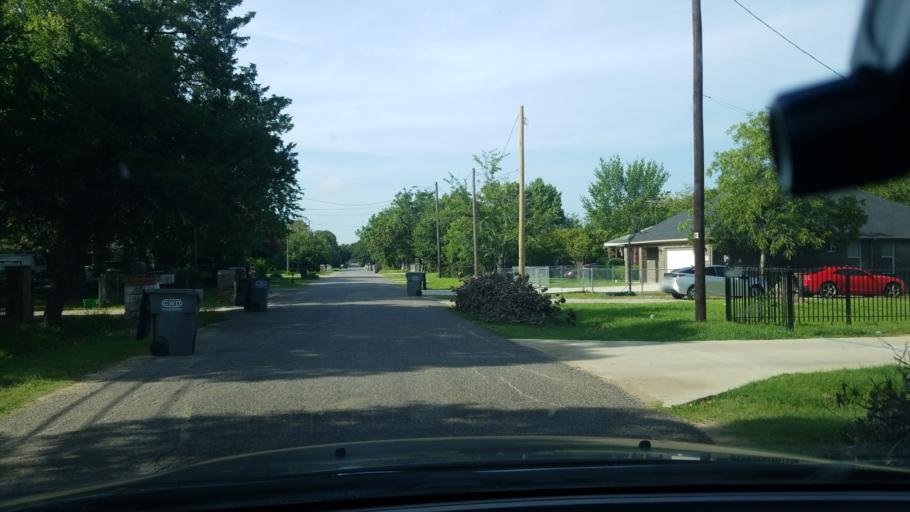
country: US
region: Texas
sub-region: Dallas County
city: Balch Springs
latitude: 32.7182
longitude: -96.6364
